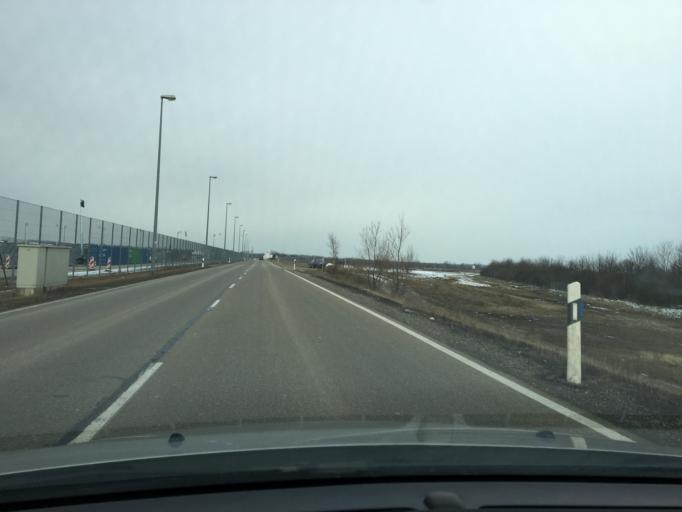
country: DE
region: Bavaria
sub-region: Upper Bavaria
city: Oberding
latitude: 48.3518
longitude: 11.8073
